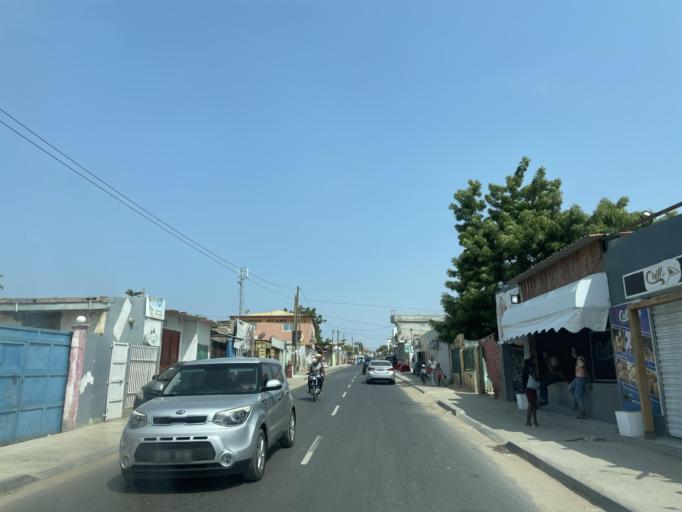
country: AO
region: Luanda
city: Luanda
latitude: -8.9278
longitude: 13.1997
